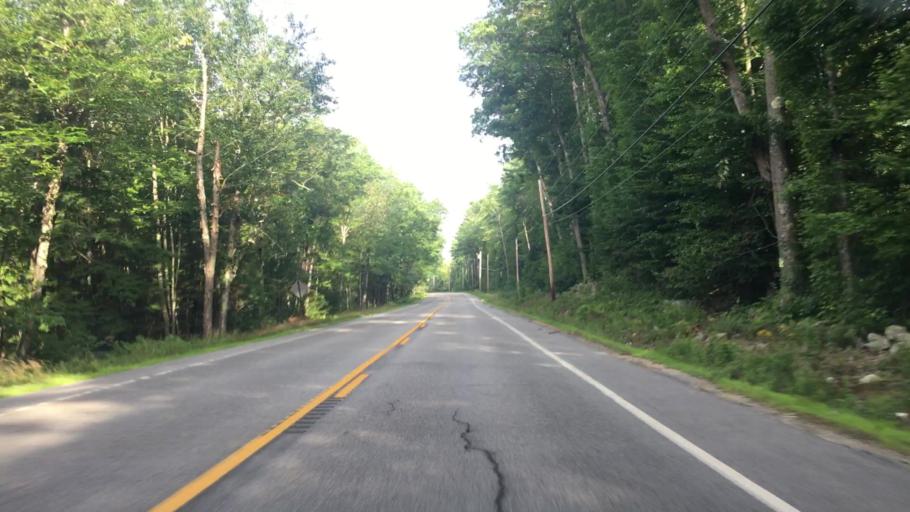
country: US
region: Maine
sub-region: York County
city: Limington
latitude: 43.7661
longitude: -70.7143
